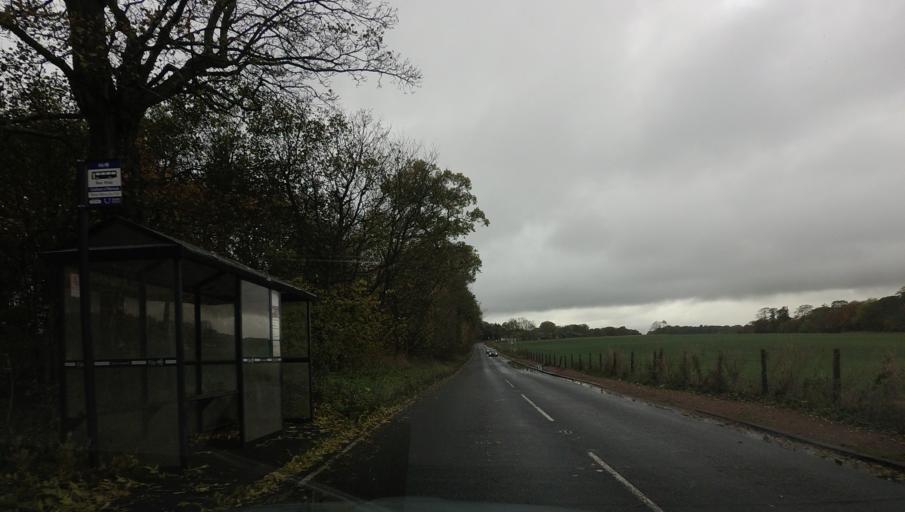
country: GB
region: Scotland
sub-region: Fife
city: East Wemyss
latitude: 56.1464
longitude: -3.0988
